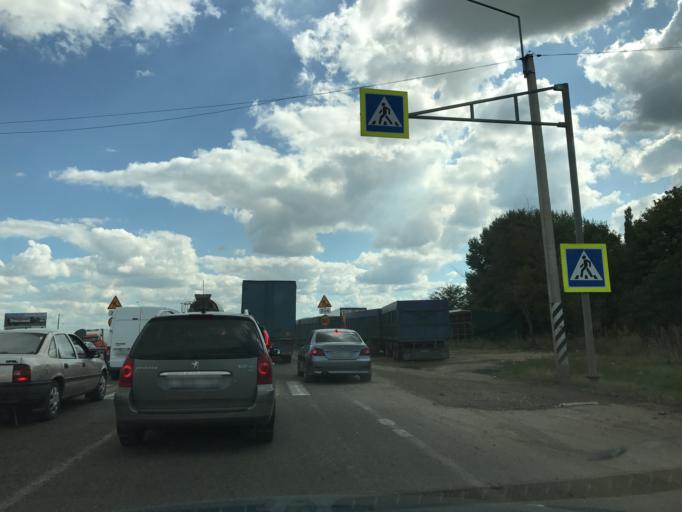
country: RU
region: Adygeya
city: Tlyustenkhabl'
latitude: 44.9595
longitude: 39.1197
